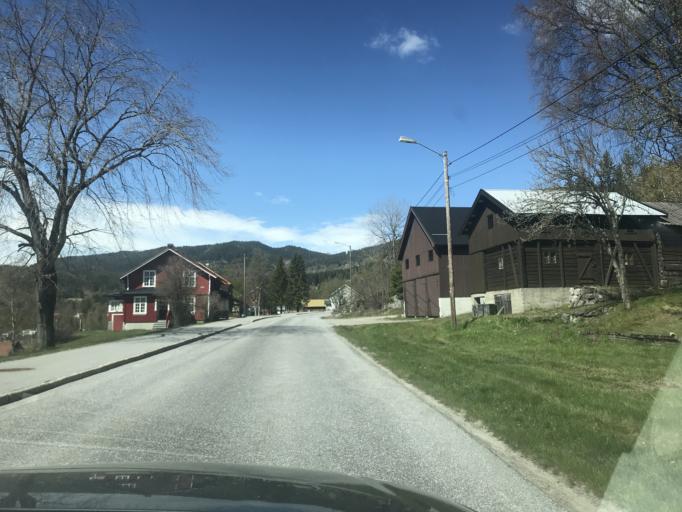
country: NO
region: Telemark
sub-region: Hjartdal
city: Sauland
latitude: 59.7515
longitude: 8.7980
